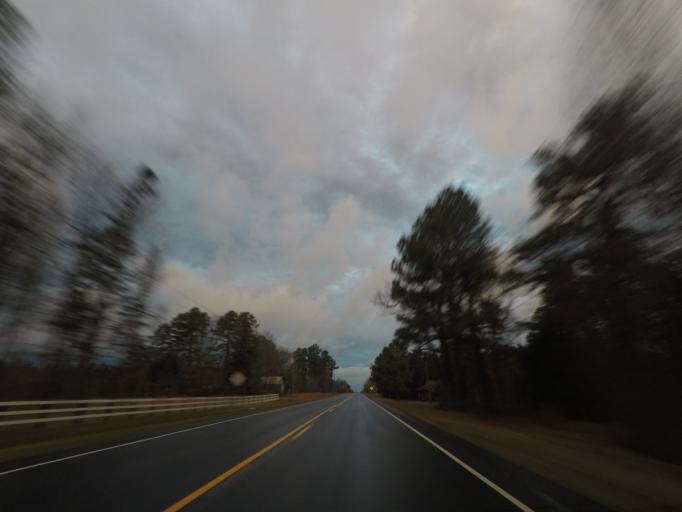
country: US
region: North Carolina
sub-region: Alamance County
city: Mebane
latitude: 36.2510
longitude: -79.1911
